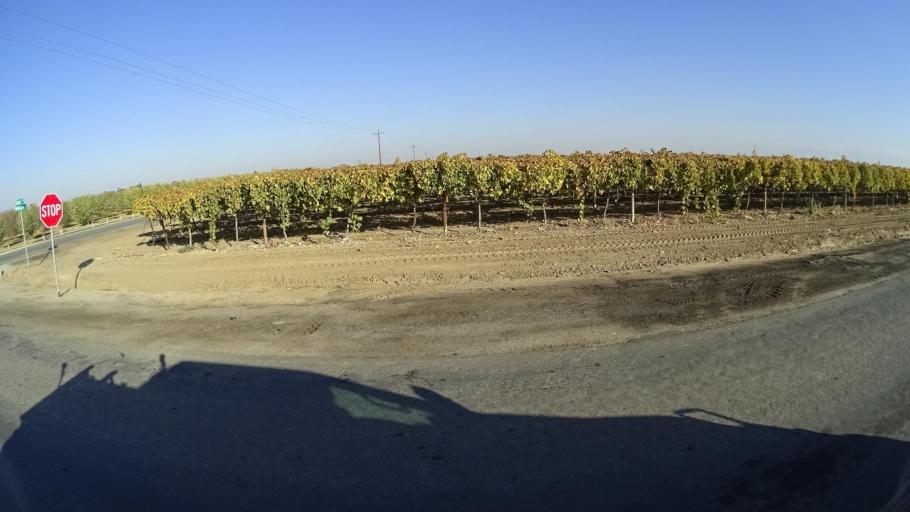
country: US
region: California
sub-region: Tulare County
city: Richgrove
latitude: 35.7687
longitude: -119.1694
